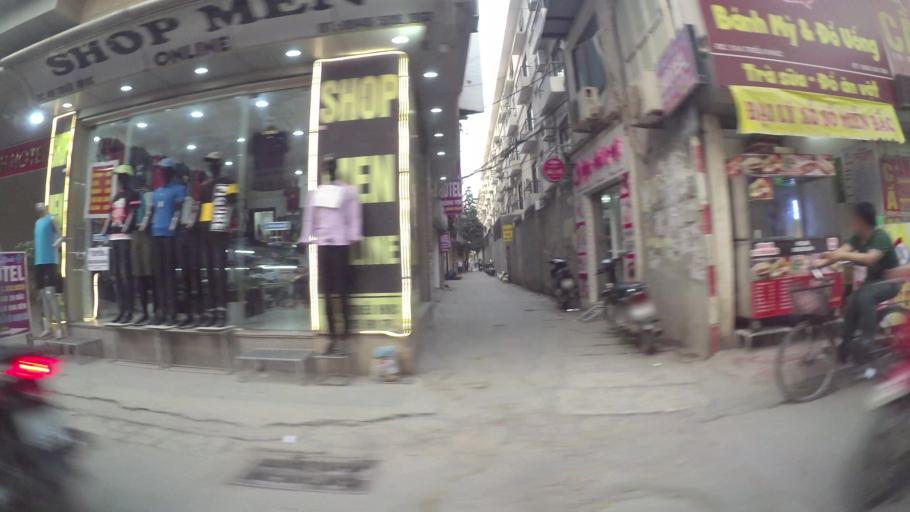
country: VN
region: Ha Noi
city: Thanh Xuan
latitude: 20.9863
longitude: 105.7981
